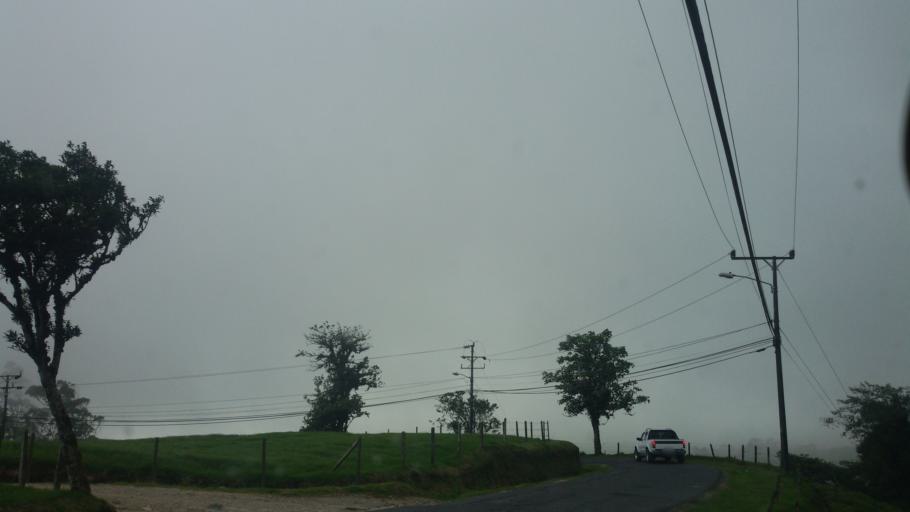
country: CR
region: San Jose
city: Ipis
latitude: 10.0052
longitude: -83.9583
